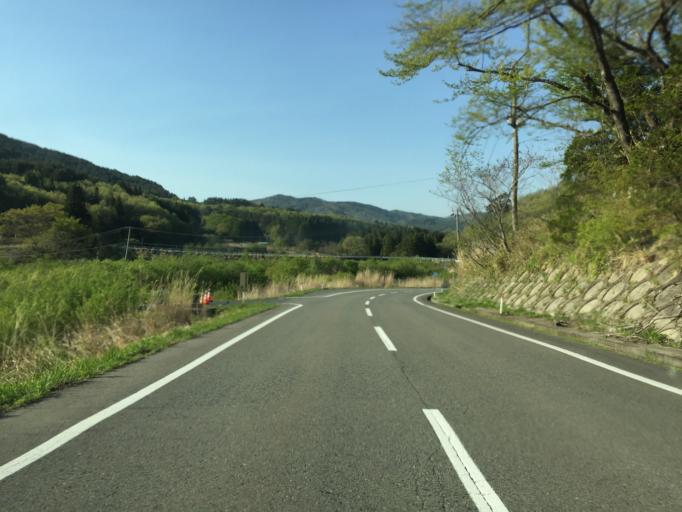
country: JP
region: Fukushima
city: Funehikimachi-funehiki
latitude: 37.5514
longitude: 140.7363
